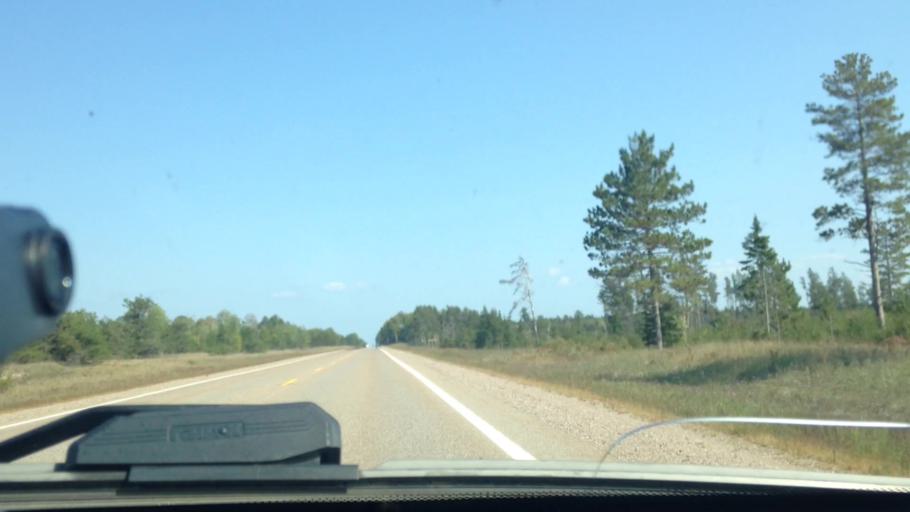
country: US
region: Michigan
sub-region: Mackinac County
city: Saint Ignace
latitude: 46.3582
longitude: -84.8840
